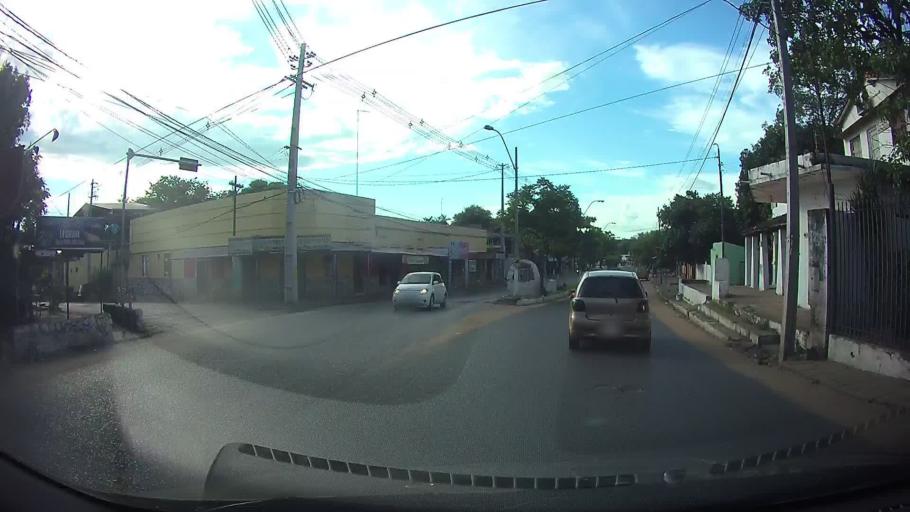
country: PY
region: Central
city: San Antonio
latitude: -25.4211
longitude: -57.5663
